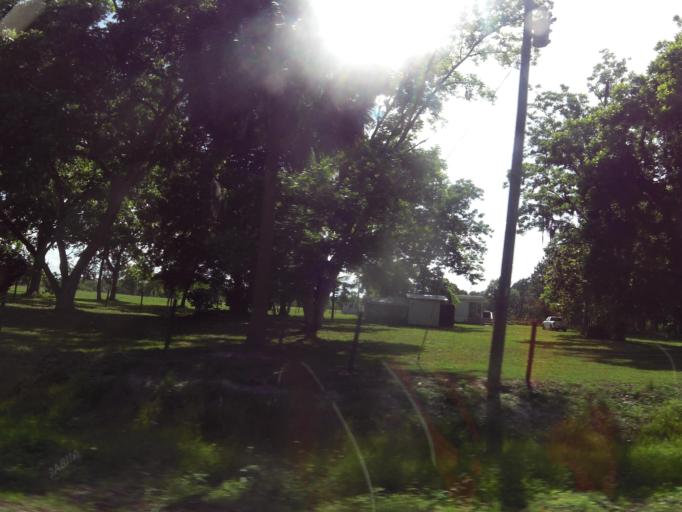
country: US
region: Florida
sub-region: Nassau County
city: Hilliard
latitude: 30.6399
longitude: -81.9025
